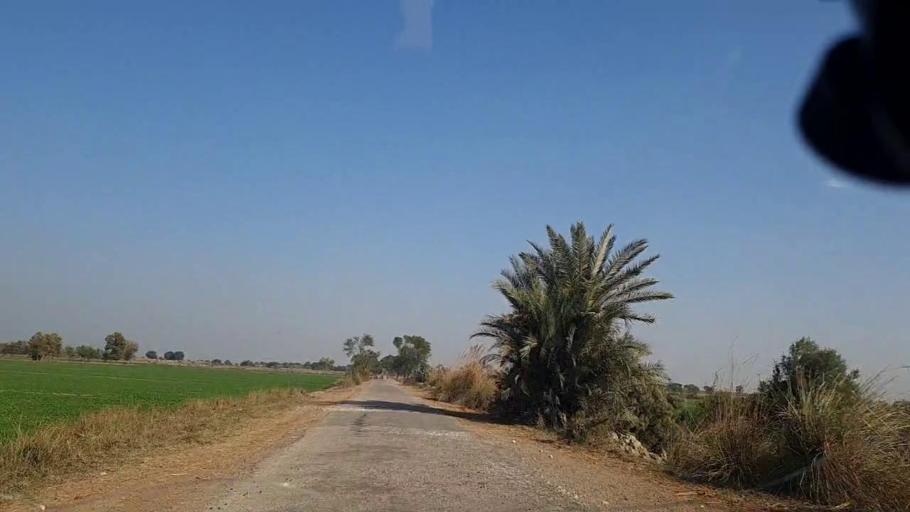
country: PK
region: Sindh
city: Khanpur
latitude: 27.6860
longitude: 69.4898
